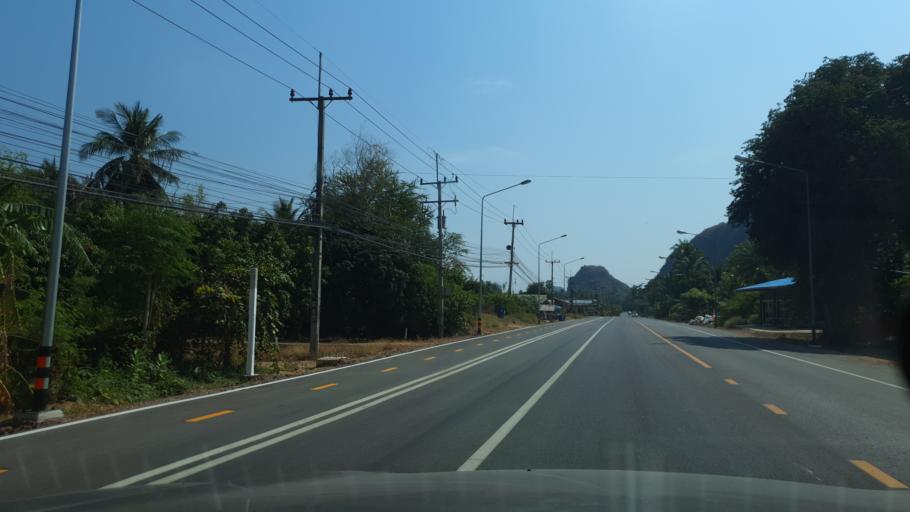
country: TH
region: Prachuap Khiri Khan
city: Sam Roi Yot
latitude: 12.2249
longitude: 99.9712
